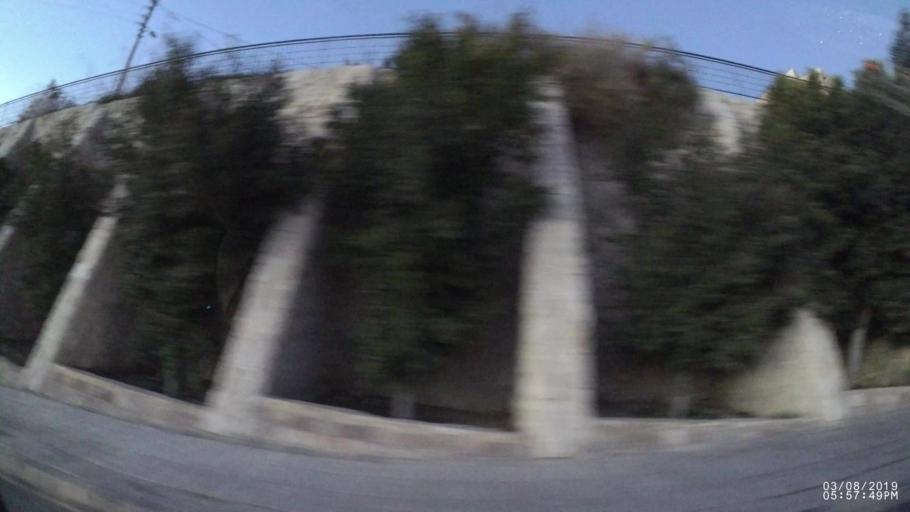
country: JO
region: Ma'an
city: Petra
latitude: 30.3236
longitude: 35.4766
